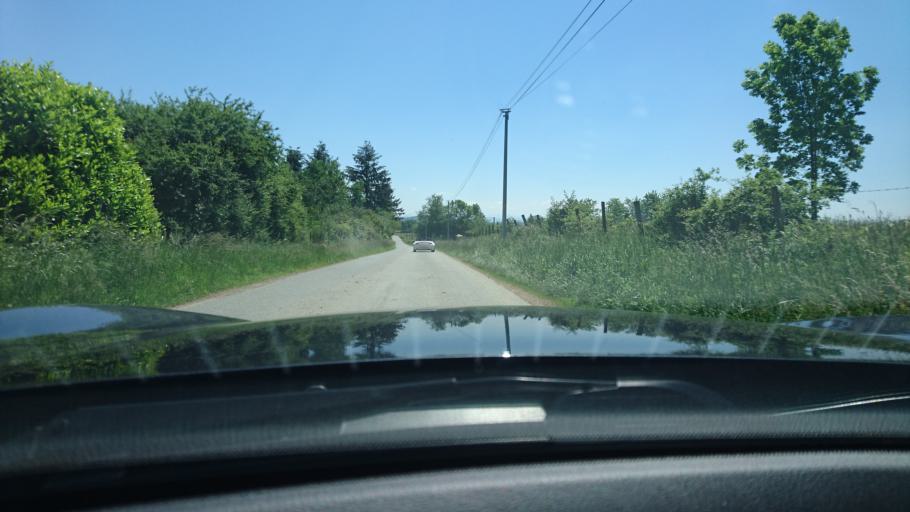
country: FR
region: Rhone-Alpes
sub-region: Departement de la Loire
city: Bussieres
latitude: 45.8250
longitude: 4.3003
